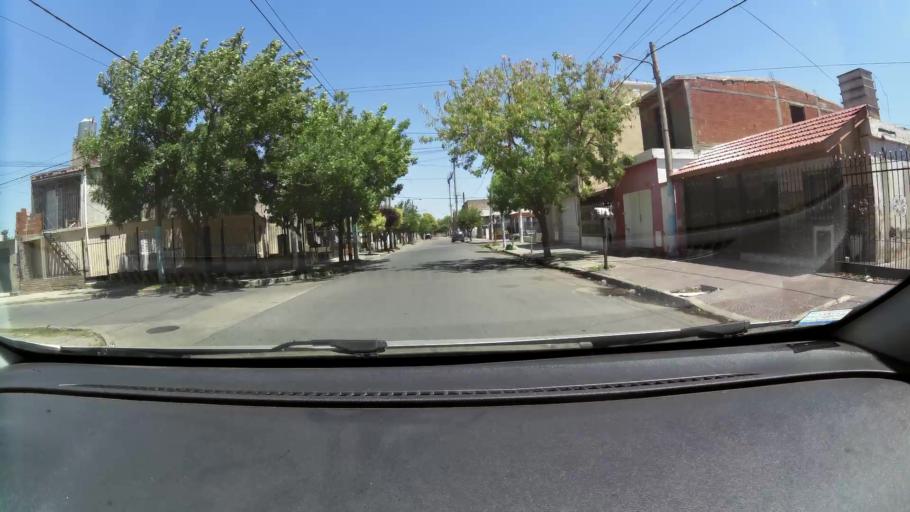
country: AR
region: Cordoba
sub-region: Departamento de Capital
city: Cordoba
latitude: -31.3880
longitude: -64.1427
